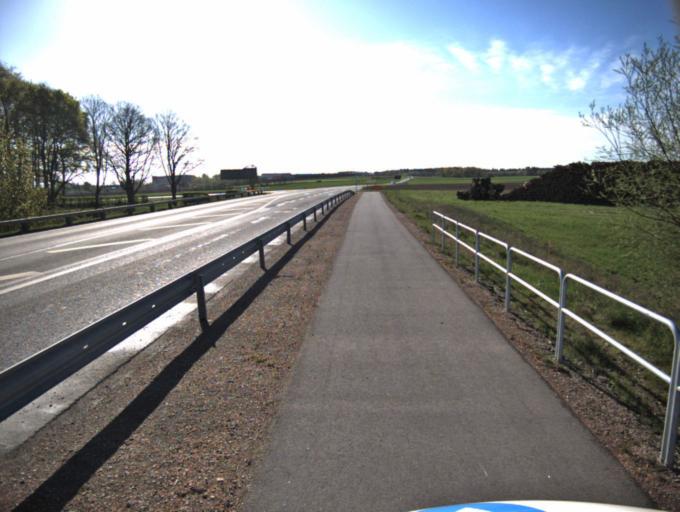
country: SE
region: Skane
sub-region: Kristianstads Kommun
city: Norra Asum
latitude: 56.0001
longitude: 14.1055
